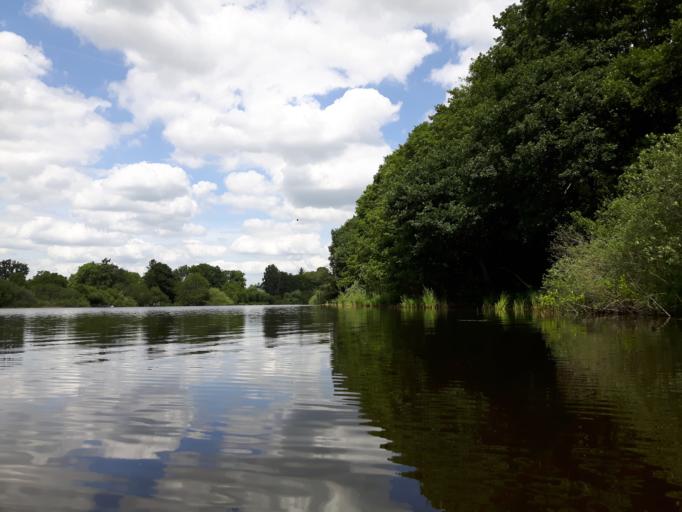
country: DE
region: Schleswig-Holstein
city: Muhbrook
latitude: 54.1531
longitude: 10.0094
